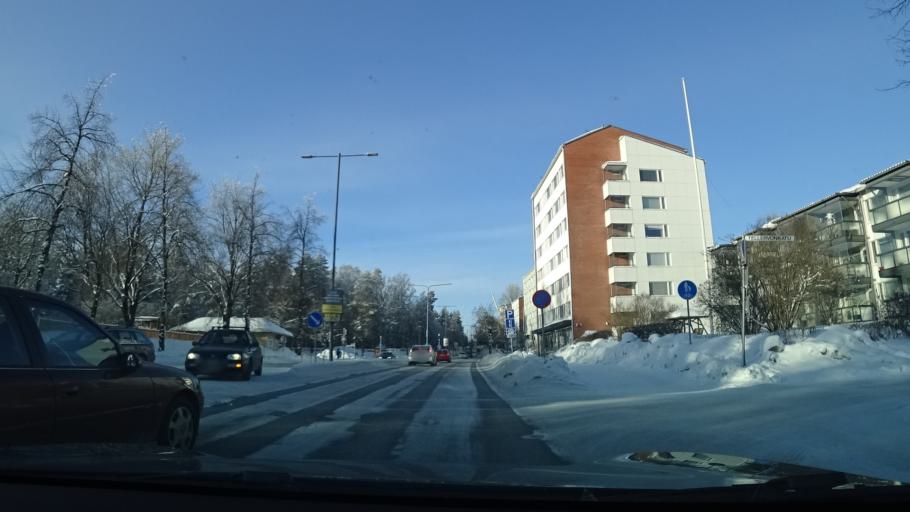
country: FI
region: South Karelia
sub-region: Lappeenranta
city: Lappeenranta
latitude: 61.0502
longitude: 28.1959
